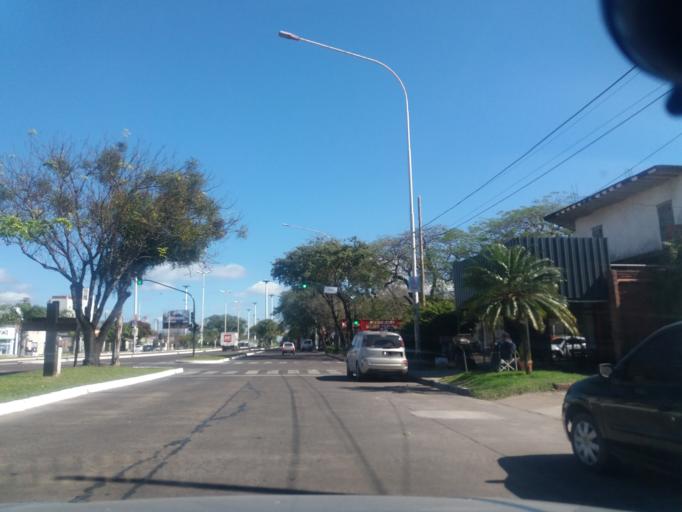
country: AR
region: Corrientes
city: Corrientes
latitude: -27.4743
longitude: -58.8471
